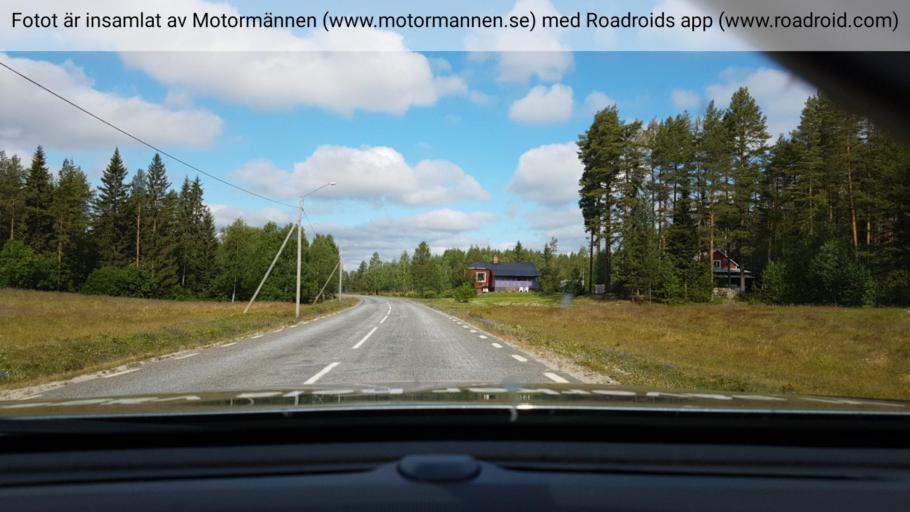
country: SE
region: Vaesterbotten
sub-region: Lycksele Kommun
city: Lycksele
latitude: 64.7634
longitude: 19.0551
